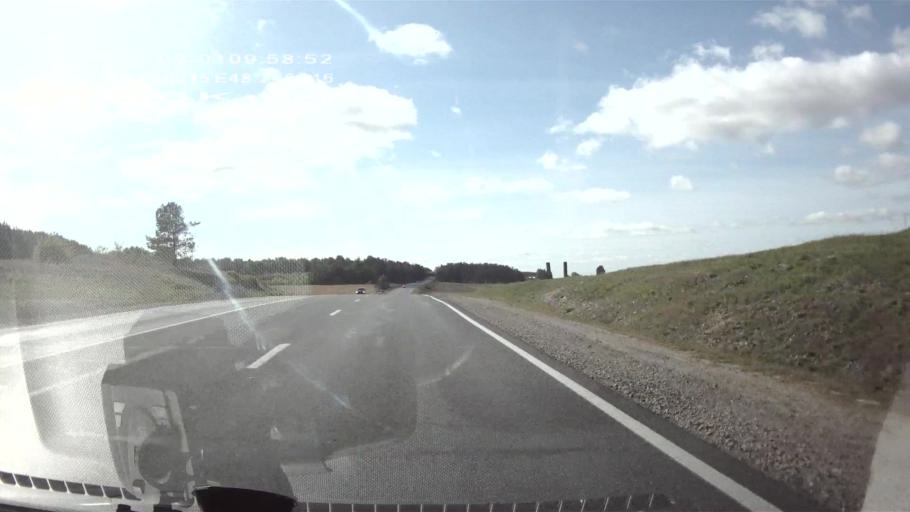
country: RU
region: Ulyanovsk
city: Krasnyy Gulyay
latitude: 54.0862
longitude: 48.2315
